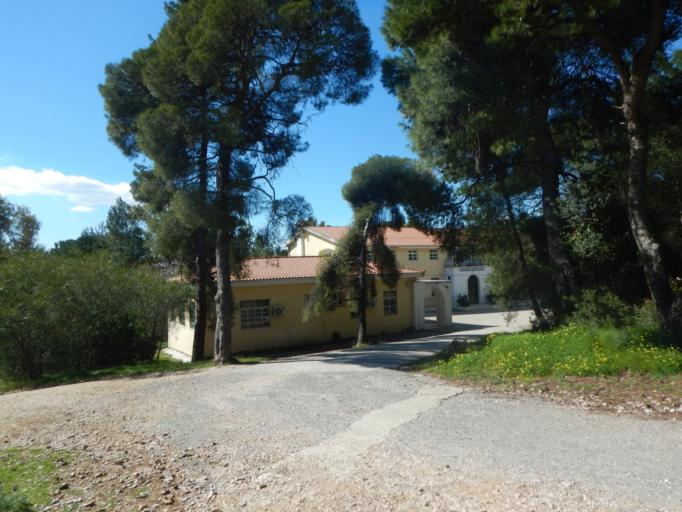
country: GR
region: Attica
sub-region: Nomarchia Athinas
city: Kifisia
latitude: 38.0652
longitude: 23.8162
